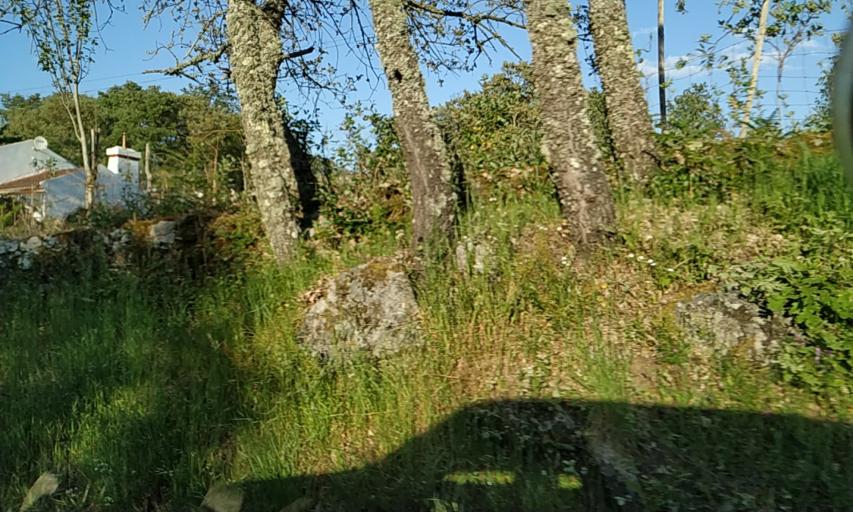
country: PT
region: Portalegre
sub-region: Marvao
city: Marvao
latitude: 39.3641
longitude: -7.4039
